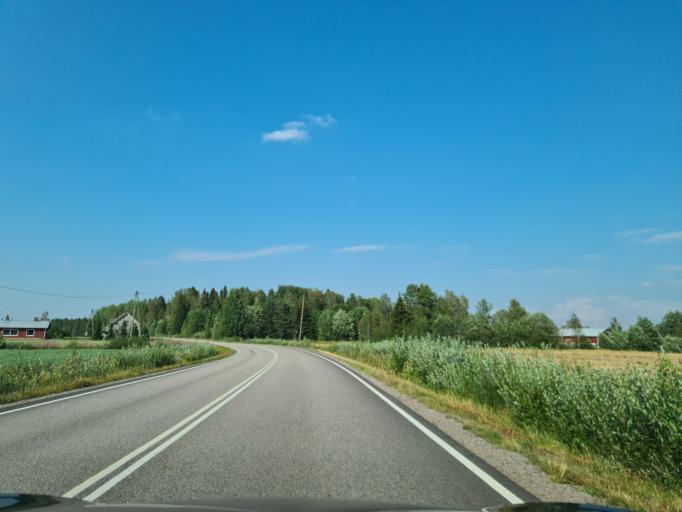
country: FI
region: Satakunta
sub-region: Pohjois-Satakunta
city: Karvia
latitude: 62.2093
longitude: 22.6048
